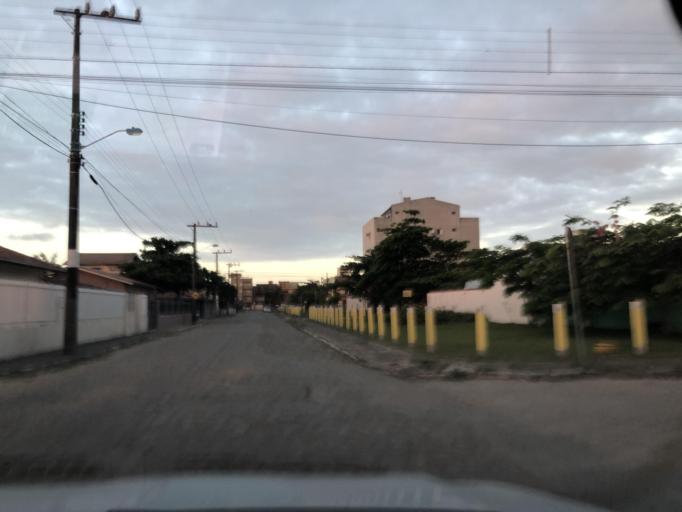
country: BR
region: Santa Catarina
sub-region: Sao Francisco Do Sul
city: Sao Francisco do Sul
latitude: -26.2296
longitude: -48.5085
